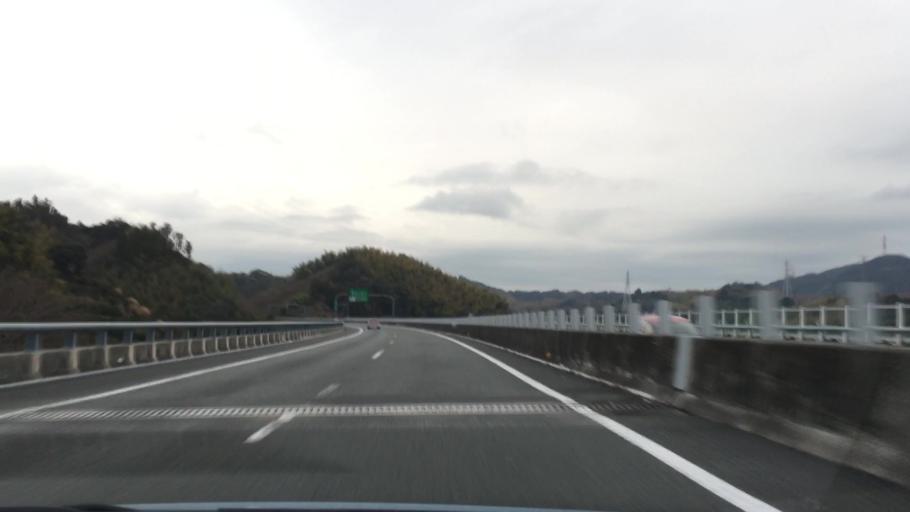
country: JP
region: Shizuoka
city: Shizuoka-shi
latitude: 35.0614
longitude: 138.4813
